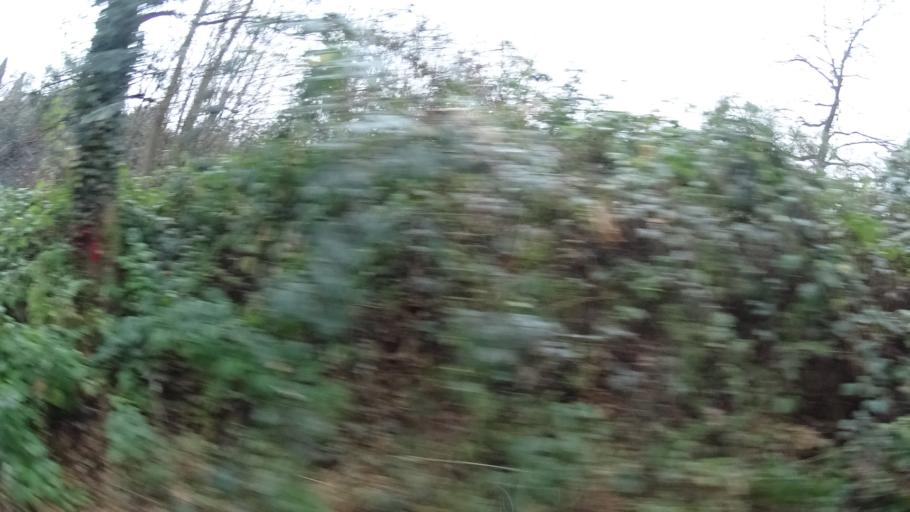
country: DE
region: Baden-Wuerttemberg
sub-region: Karlsruhe Region
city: Heidelberg
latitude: 49.4151
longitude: 8.7354
